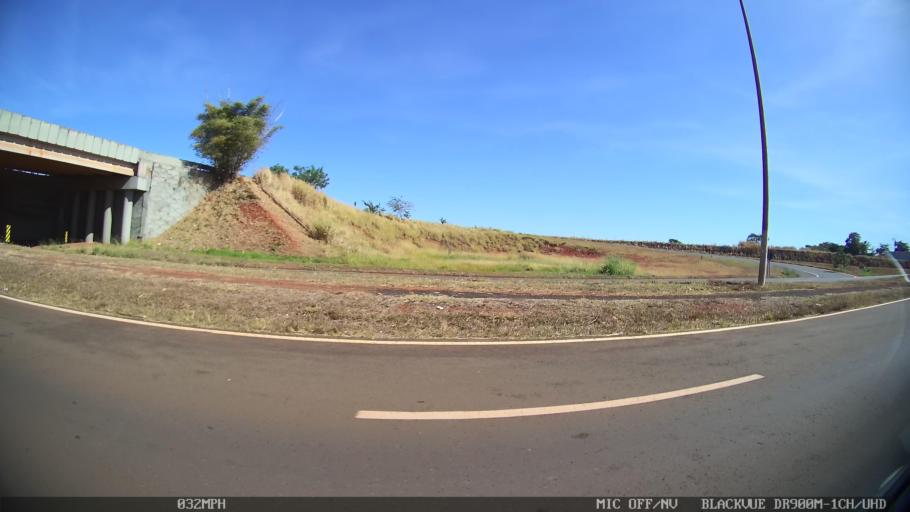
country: BR
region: Sao Paulo
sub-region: Barretos
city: Barretos
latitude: -20.5262
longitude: -48.5902
